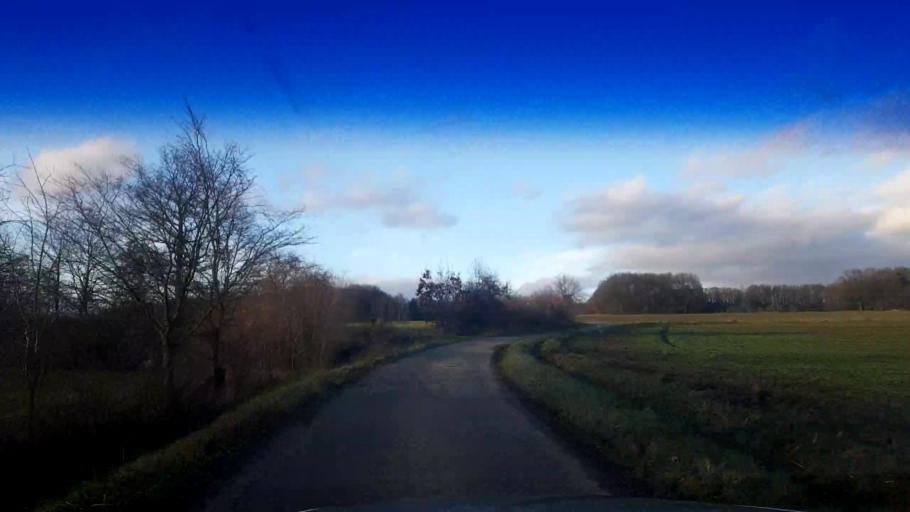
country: DE
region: Bavaria
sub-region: Upper Franconia
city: Buttenheim
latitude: 49.8144
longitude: 11.0369
